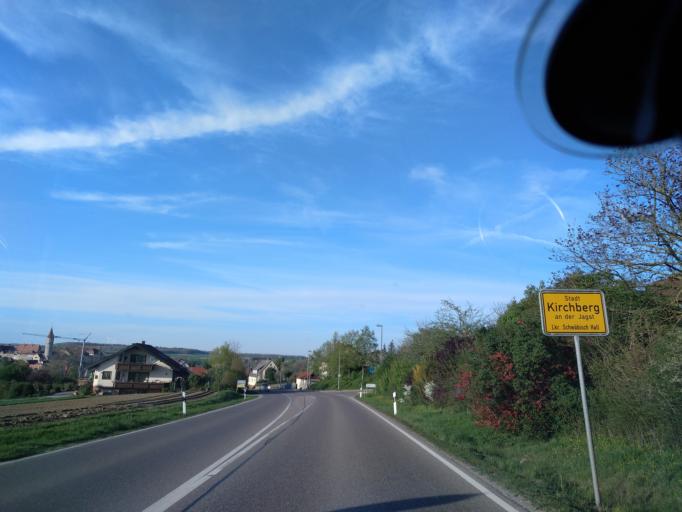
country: DE
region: Baden-Wuerttemberg
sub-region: Regierungsbezirk Stuttgart
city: Kirchberg an der Jagst
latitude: 49.1988
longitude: 9.9806
